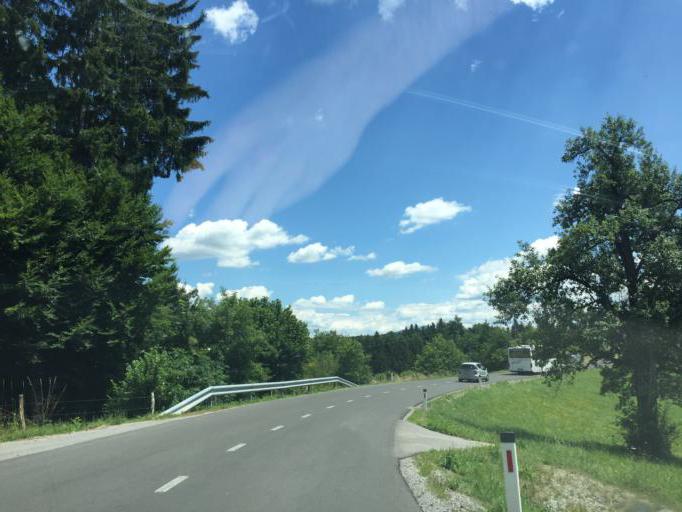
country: SI
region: Postojna
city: Postojna
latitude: 45.8183
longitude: 14.1419
